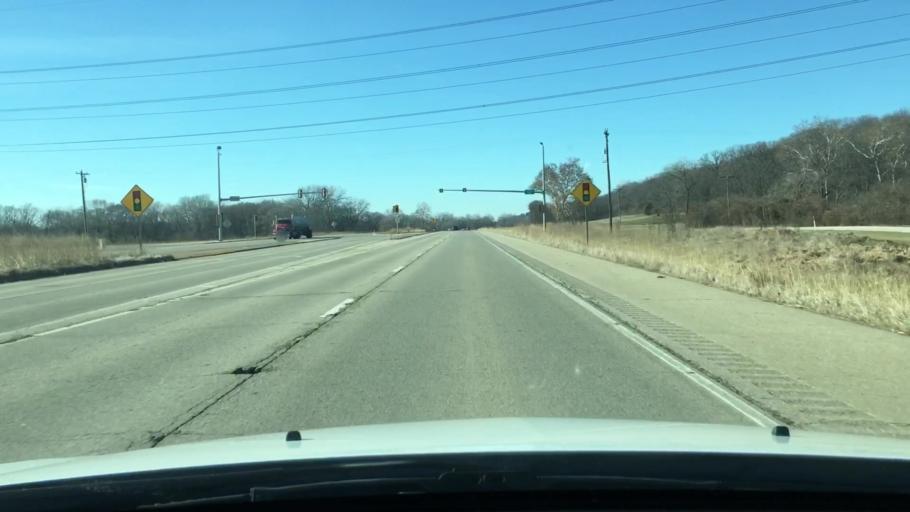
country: US
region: Illinois
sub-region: Peoria County
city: Glasford
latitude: 40.5617
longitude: -89.7501
